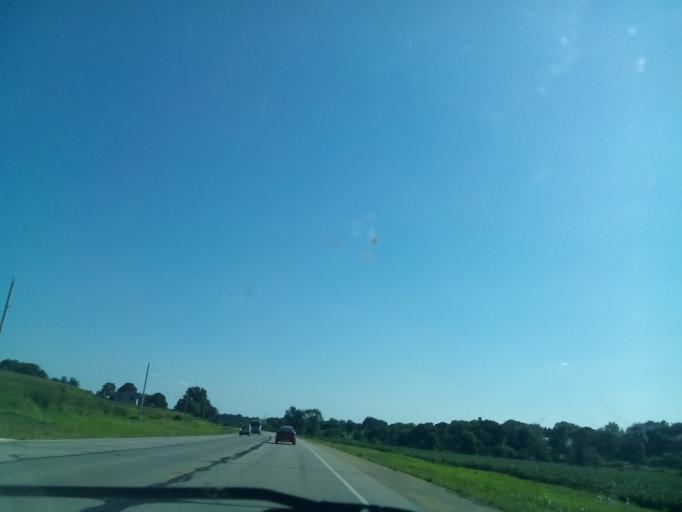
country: US
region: Wisconsin
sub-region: Green County
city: New Glarus
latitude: 42.8400
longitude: -89.6344
